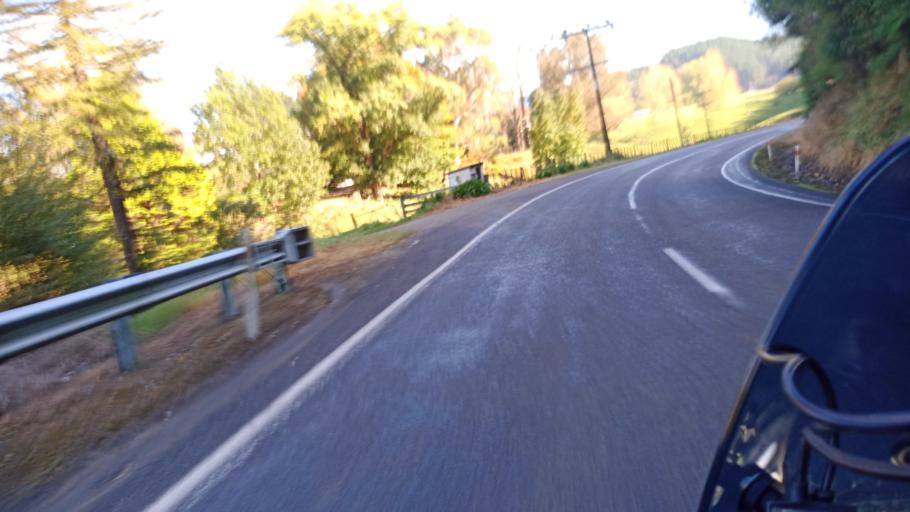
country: NZ
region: Hawke's Bay
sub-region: Wairoa District
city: Wairoa
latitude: -38.9252
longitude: 177.2728
